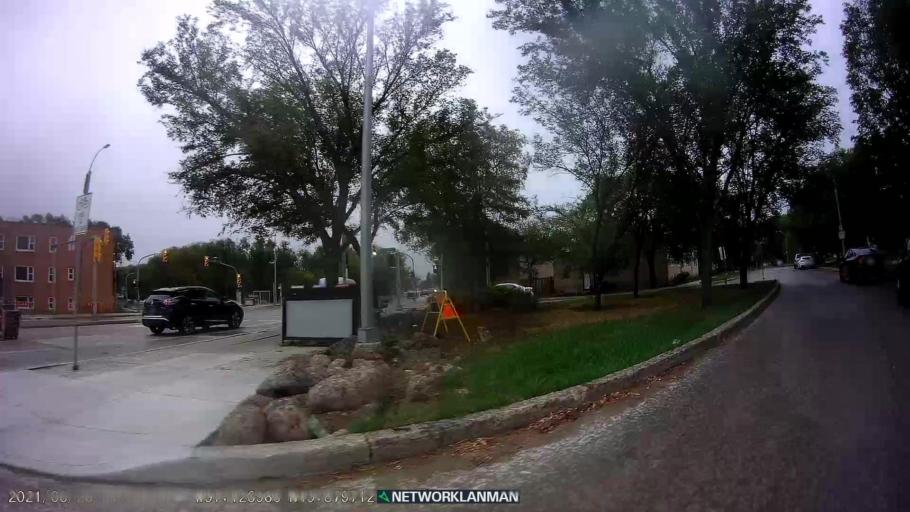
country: CA
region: Manitoba
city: Winnipeg
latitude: 49.8797
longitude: -97.1268
